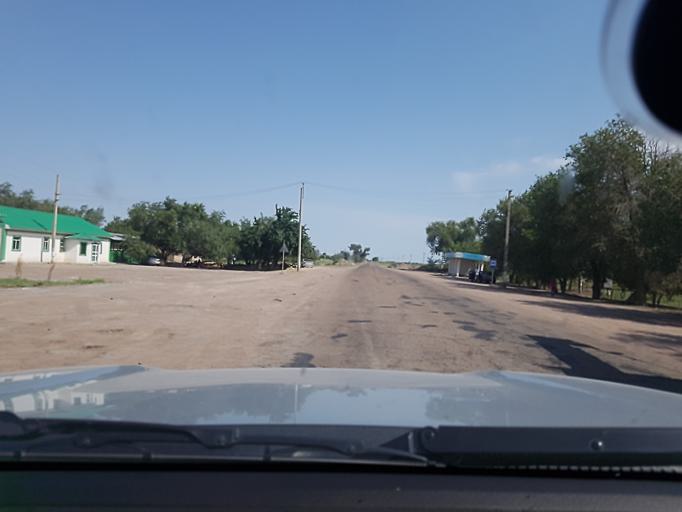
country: UZ
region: Karakalpakstan
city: Khujayli
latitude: 42.2352
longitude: 59.4535
